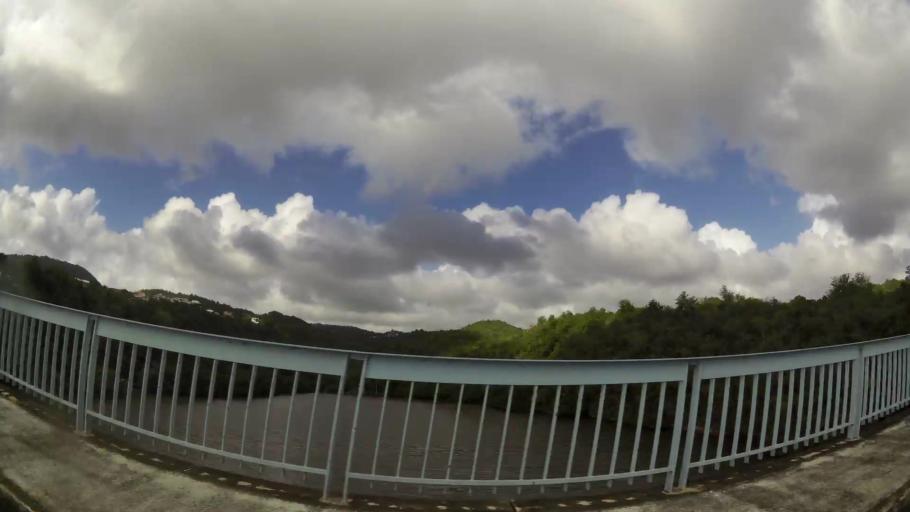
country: MQ
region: Martinique
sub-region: Martinique
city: Sainte-Luce
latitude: 14.4693
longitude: -60.9170
